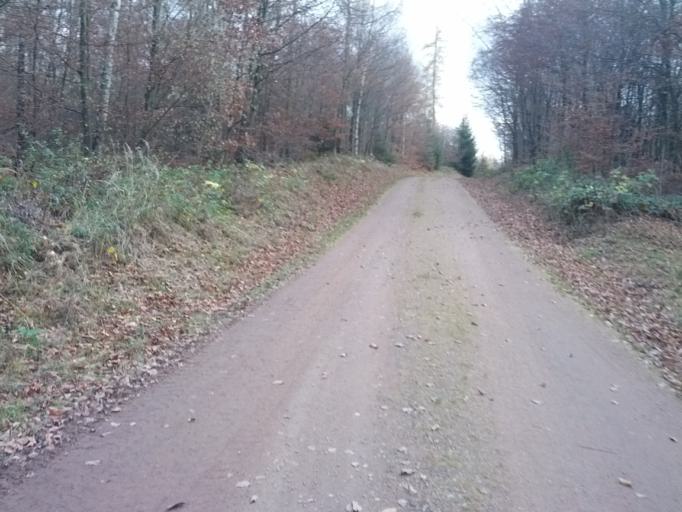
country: DE
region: Thuringia
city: Wolfsburg-Unkeroda
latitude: 50.9499
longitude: 10.2739
